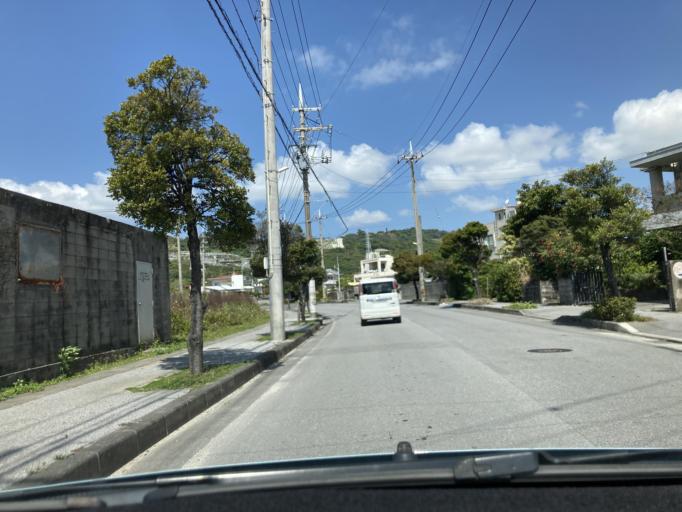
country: JP
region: Okinawa
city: Ginowan
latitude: 26.2614
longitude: 127.7911
